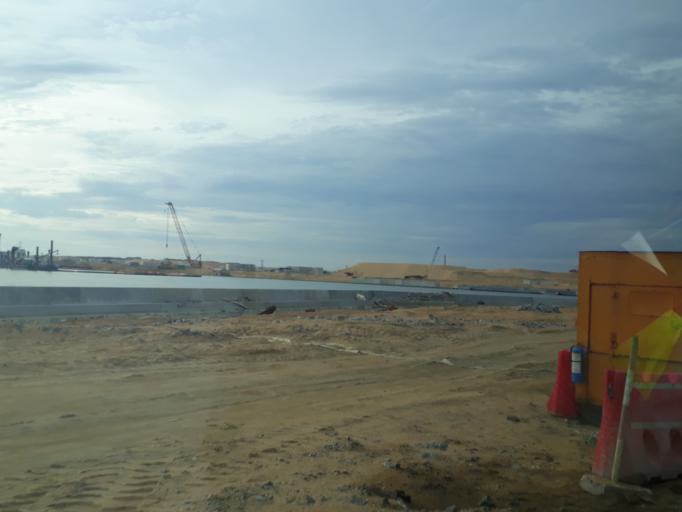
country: LK
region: Western
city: Colombo
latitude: 6.9263
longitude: 79.8408
